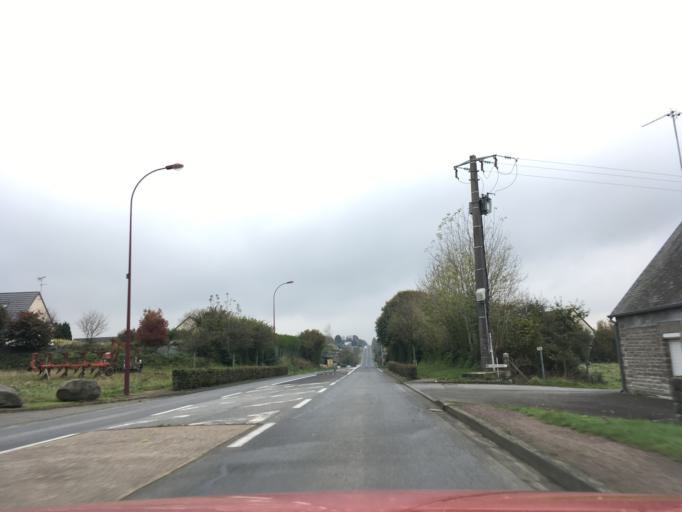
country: FR
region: Lower Normandy
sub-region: Departement de la Manche
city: Villedieu-les-Poeles
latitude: 48.8447
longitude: -1.2752
